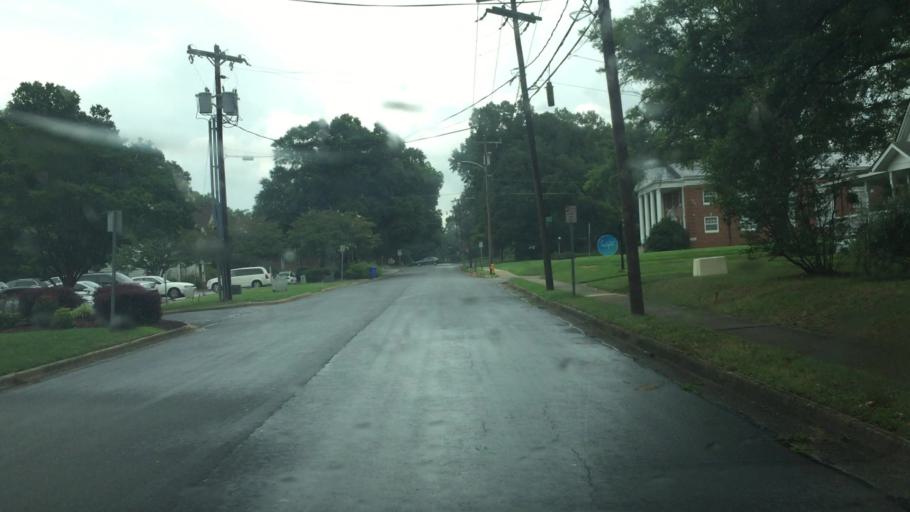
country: US
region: North Carolina
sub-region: Iredell County
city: Mooresville
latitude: 35.5809
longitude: -80.8025
